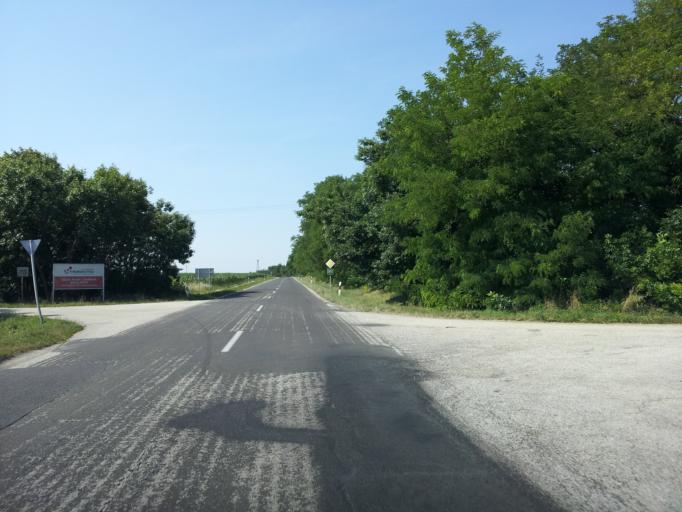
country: HU
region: Fejer
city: Lovasbereny
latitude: 47.2864
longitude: 18.5293
